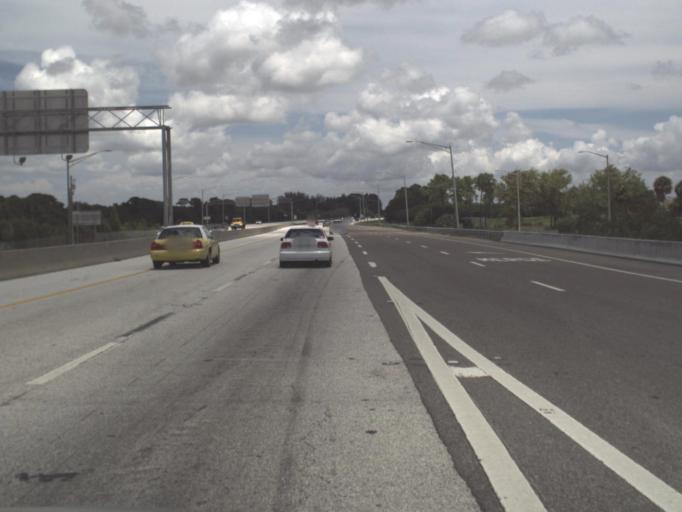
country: US
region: Florida
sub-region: Pinellas County
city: South Highpoint
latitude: 27.9126
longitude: -82.7005
